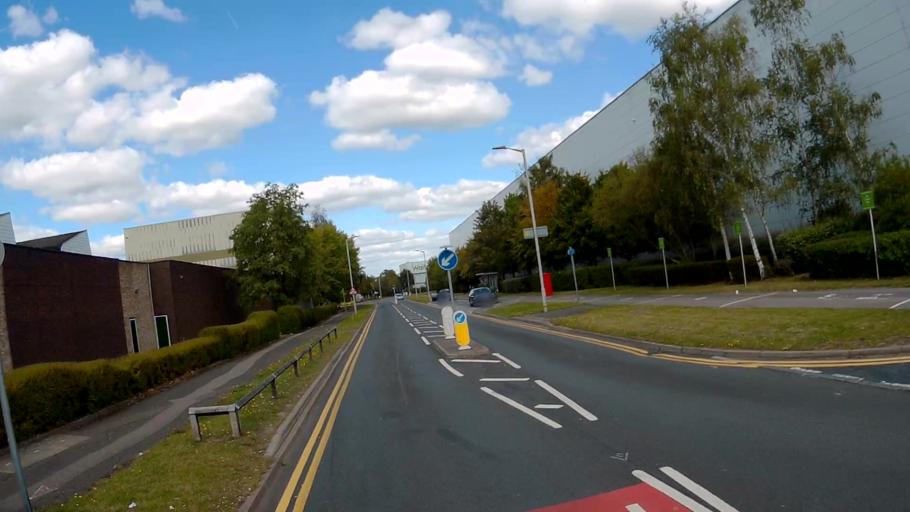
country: GB
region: England
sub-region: Bracknell Forest
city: Bracknell
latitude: 51.4097
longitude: -0.7743
